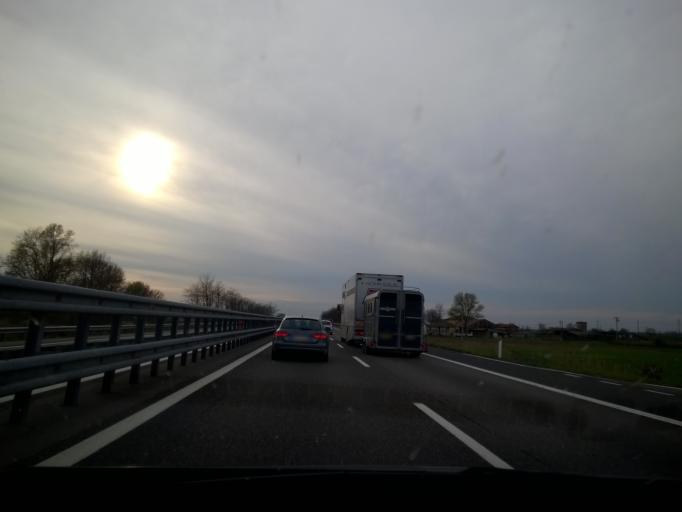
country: IT
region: Emilia-Romagna
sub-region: Provincia di Piacenza
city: Sarmato
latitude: 45.0689
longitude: 9.5061
